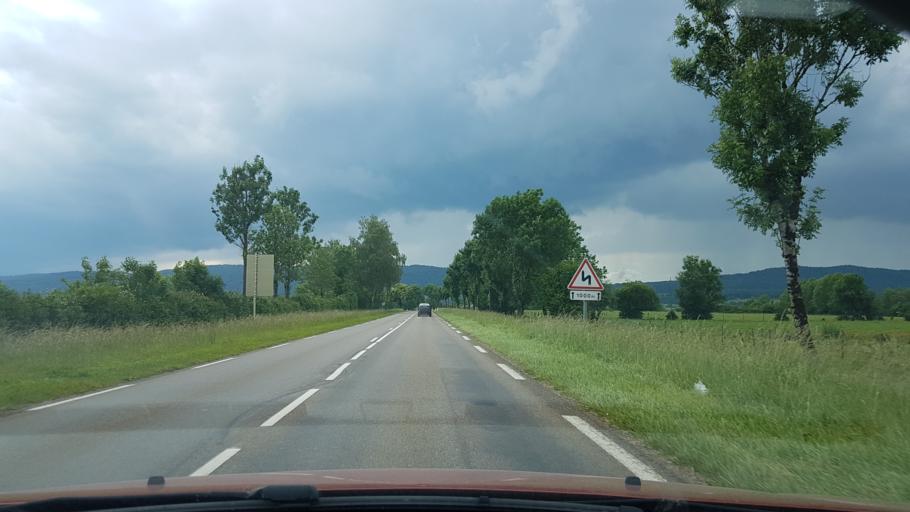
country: FR
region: Franche-Comte
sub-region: Departement du Jura
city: Clairvaux-les-Lacs
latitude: 46.5894
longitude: 5.7121
